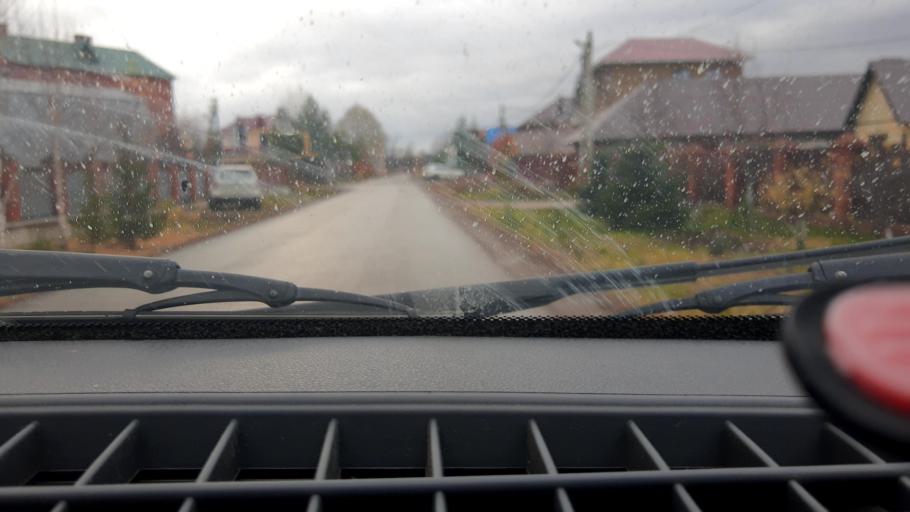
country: RU
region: Bashkortostan
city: Mikhaylovka
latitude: 54.8073
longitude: 55.9395
